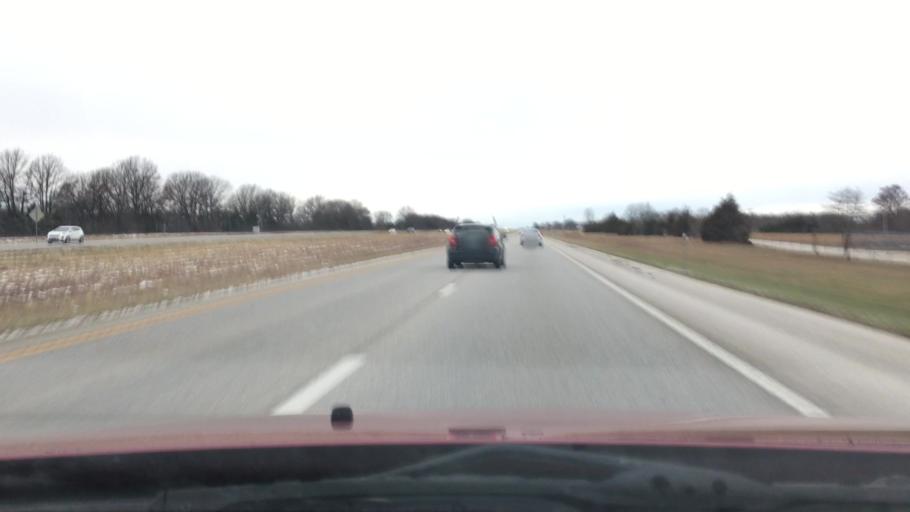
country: US
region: Missouri
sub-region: Webster County
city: Seymour
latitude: 37.1699
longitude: -92.8292
